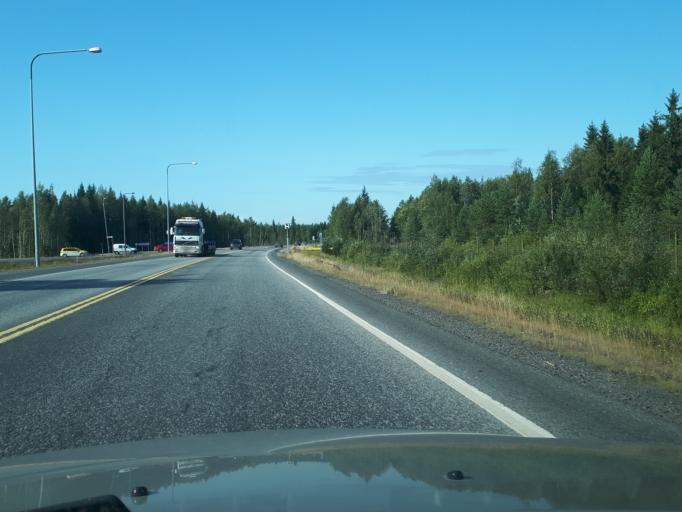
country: FI
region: Northern Ostrobothnia
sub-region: Oulunkaari
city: Ii
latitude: 65.2636
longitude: 25.3649
